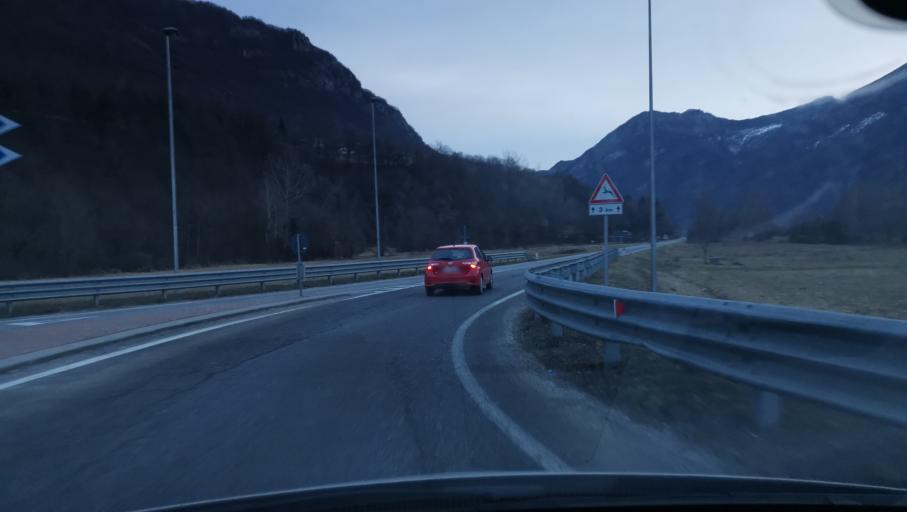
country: IT
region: Piedmont
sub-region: Provincia di Cuneo
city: Valloriate
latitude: 44.3128
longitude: 7.3450
